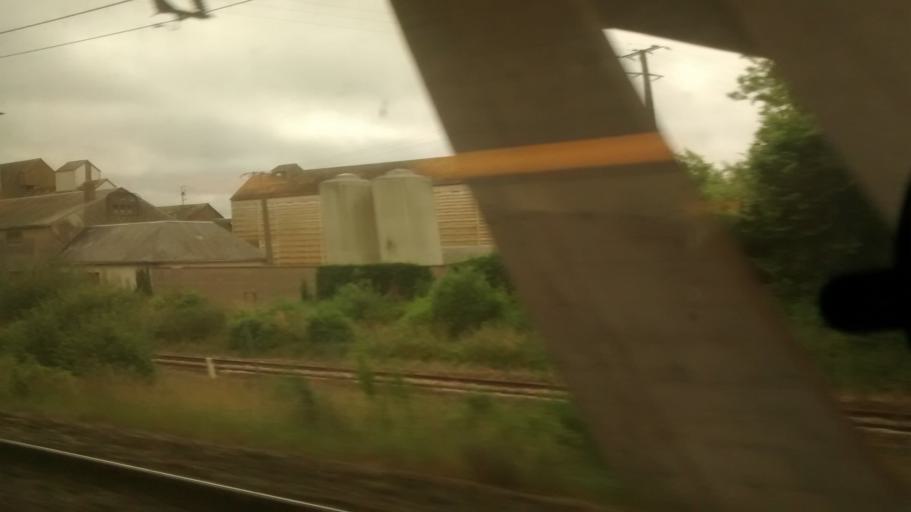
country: FR
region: Centre
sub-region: Departement d'Eure-et-Loir
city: Dammarie
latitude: 48.2329
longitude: 1.4891
